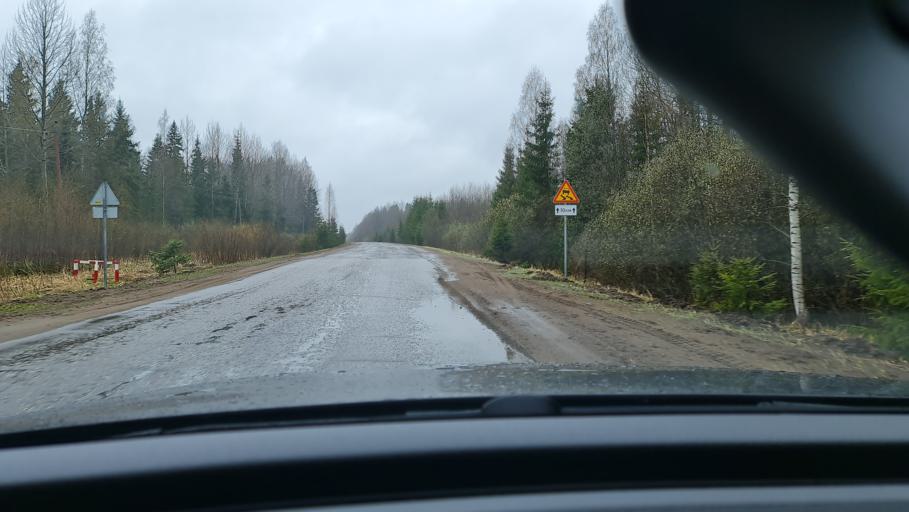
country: RU
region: Novgorod
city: Kresttsy
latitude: 58.0307
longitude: 32.8159
